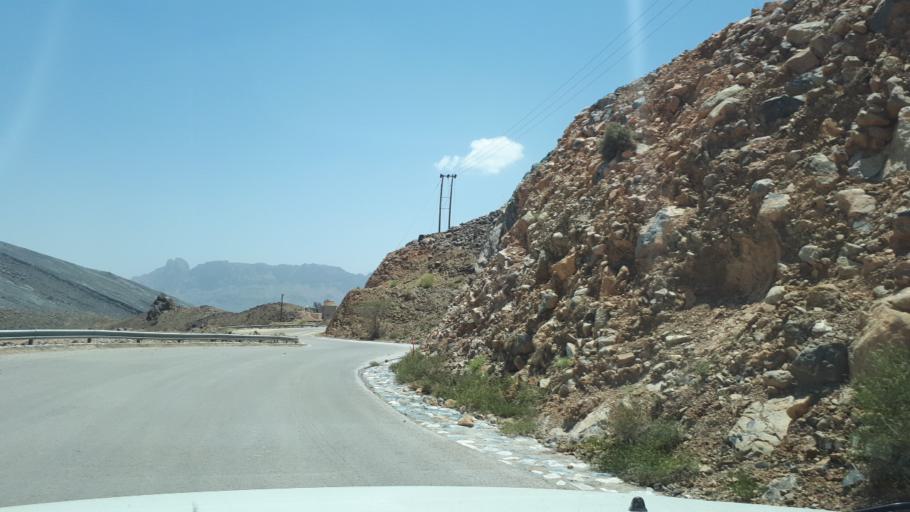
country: OM
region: Muhafazat ad Dakhiliyah
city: Bahla'
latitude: 23.2182
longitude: 57.1459
